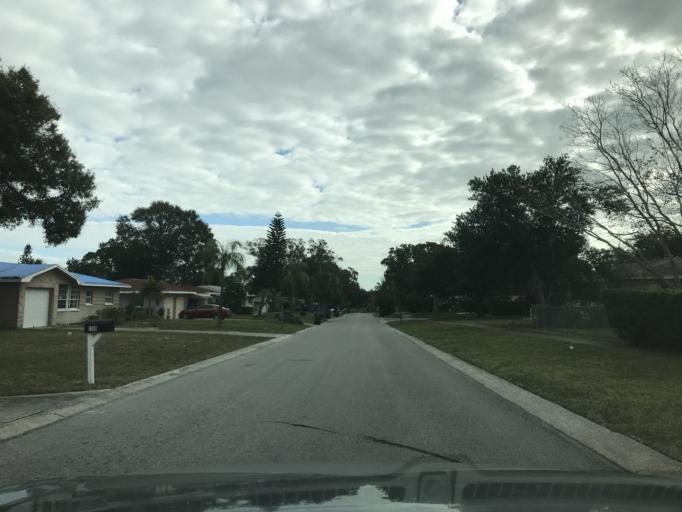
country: US
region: Florida
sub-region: Pinellas County
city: Largo
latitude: 27.9311
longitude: -82.7833
